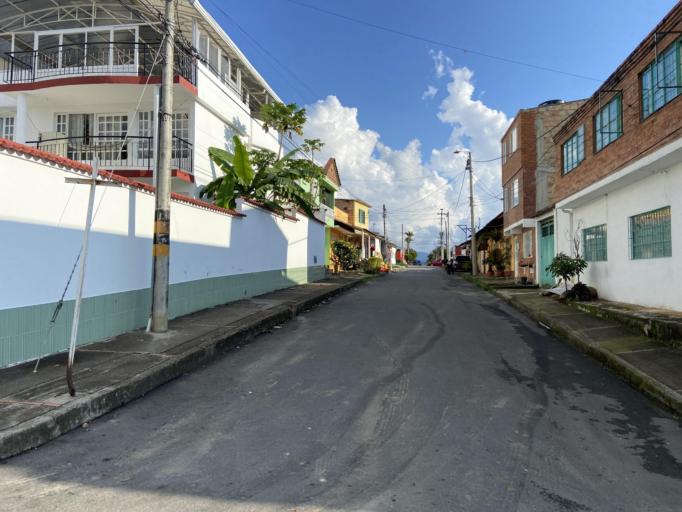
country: CO
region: Cundinamarca
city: San Antonio del Tequendama
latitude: 4.6324
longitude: -74.4561
